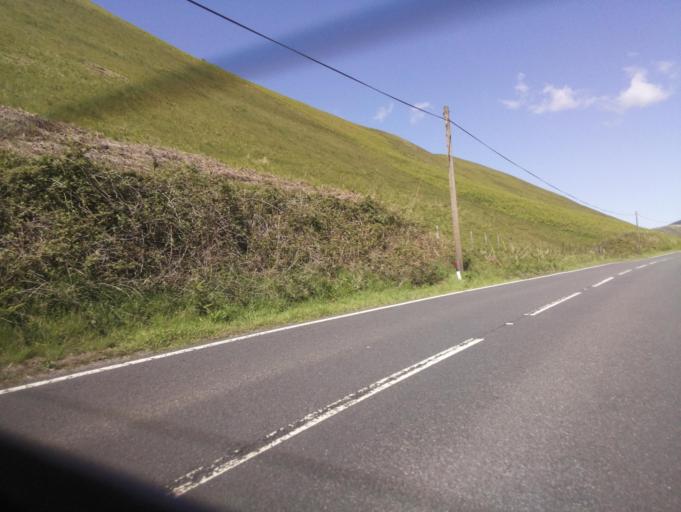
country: GB
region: Scotland
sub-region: Dumfries and Galloway
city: Langholm
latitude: 55.2367
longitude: -2.9746
